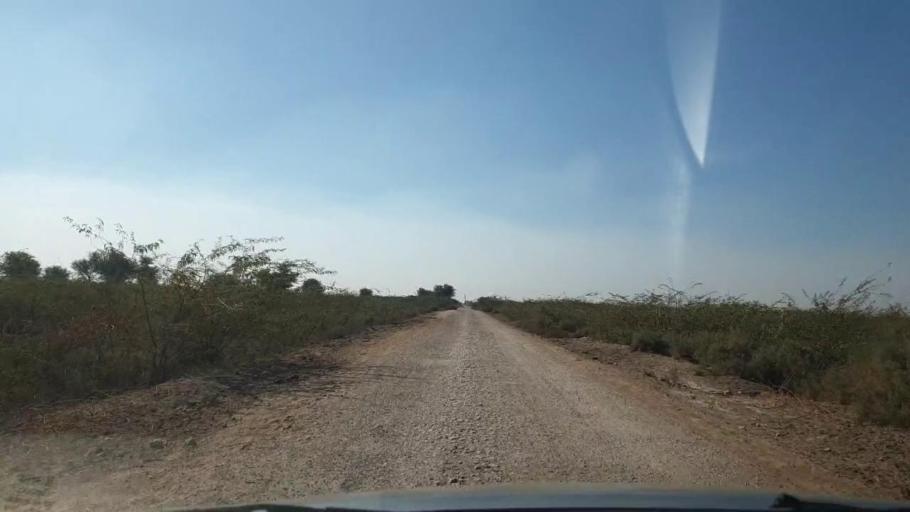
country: PK
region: Sindh
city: Jhol
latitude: 25.8128
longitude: 69.0112
